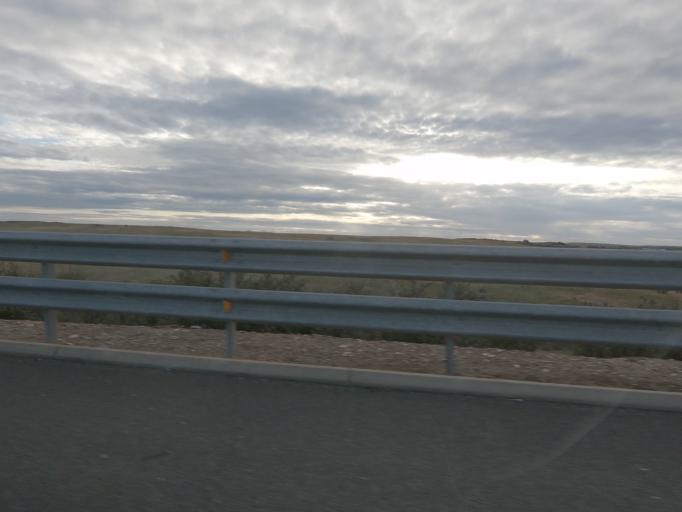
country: ES
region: Extremadura
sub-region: Provincia de Caceres
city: Caceres
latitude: 39.4893
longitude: -6.4365
